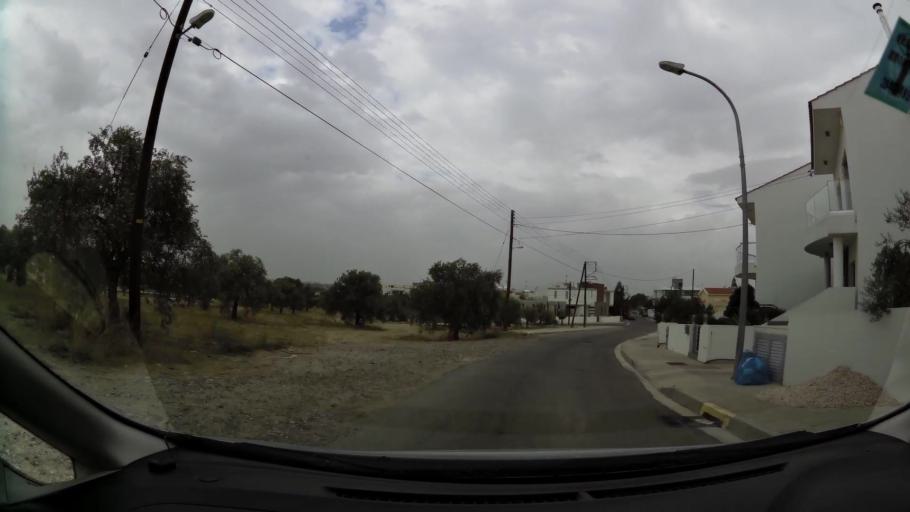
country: CY
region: Lefkosia
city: Geri
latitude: 35.0995
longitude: 33.3724
